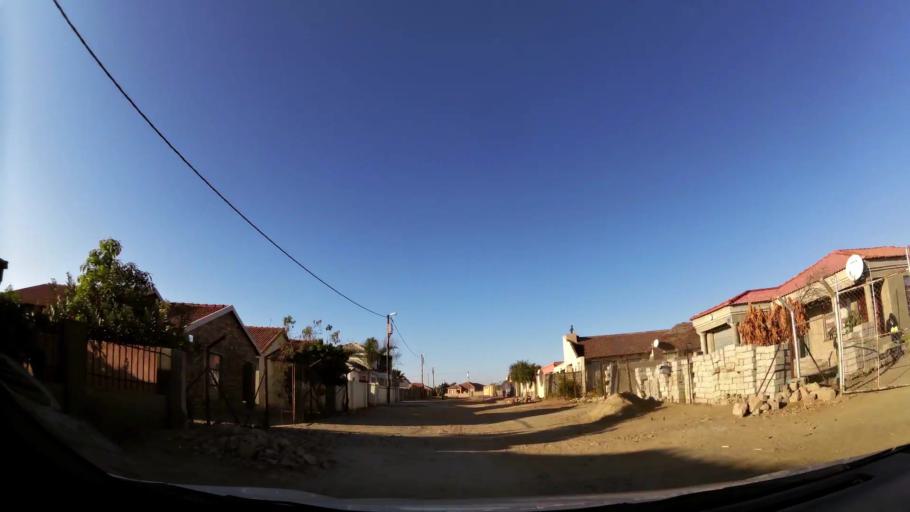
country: ZA
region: Limpopo
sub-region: Capricorn District Municipality
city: Polokwane
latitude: -23.8438
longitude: 29.3579
